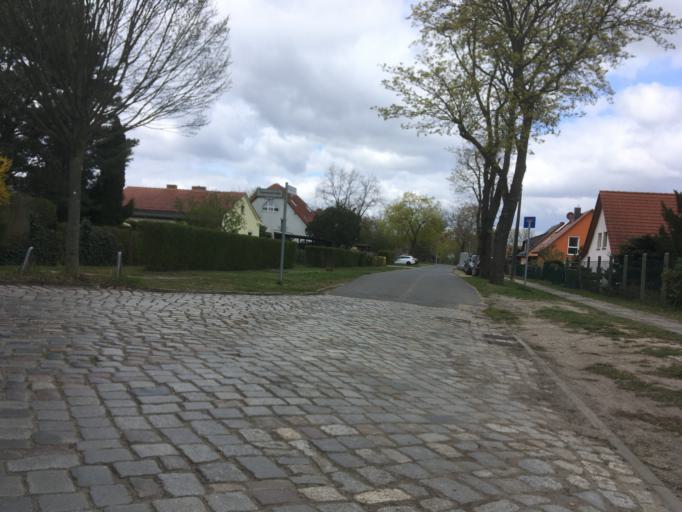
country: DE
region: Berlin
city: Altglienicke
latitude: 52.4142
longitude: 13.5555
